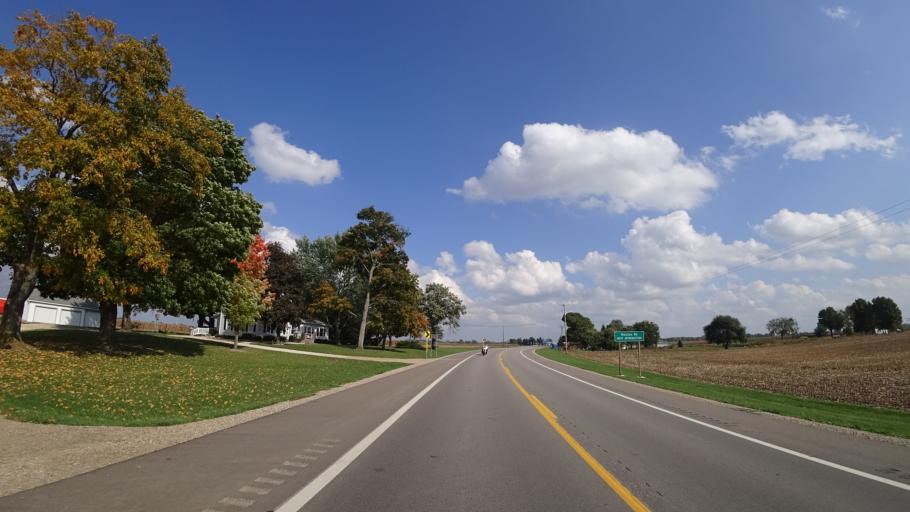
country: US
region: Michigan
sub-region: Calhoun County
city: Athens
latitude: 42.0575
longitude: -85.2765
